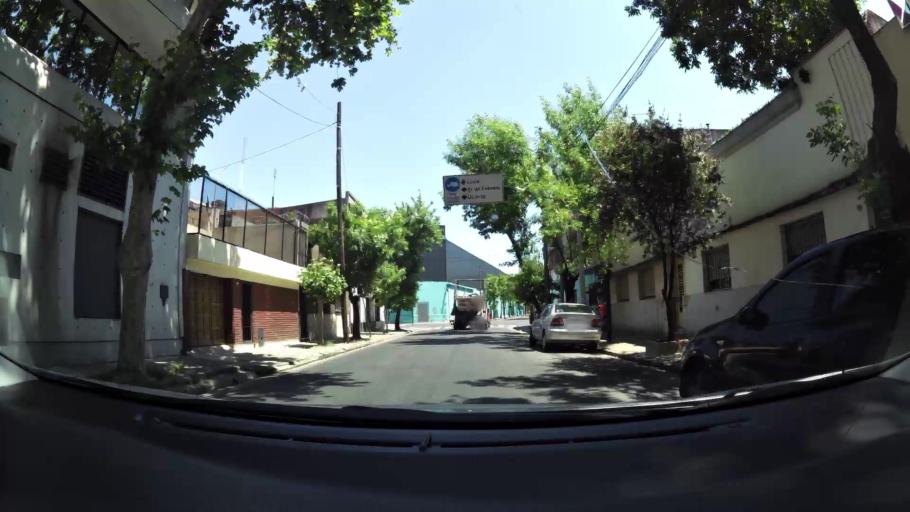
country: AR
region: Buenos Aires
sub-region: Partido de Avellaneda
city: Avellaneda
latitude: -34.6556
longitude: -58.3882
